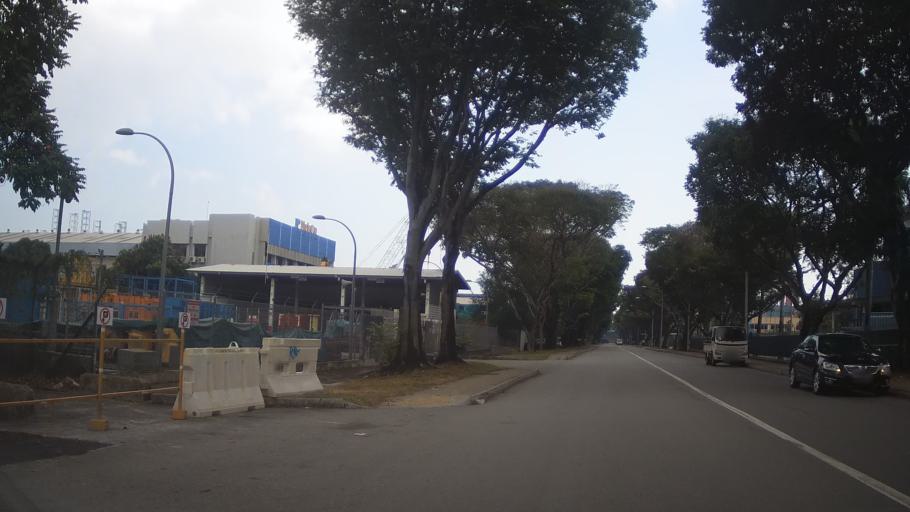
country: SG
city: Singapore
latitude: 1.3086
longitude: 103.6757
